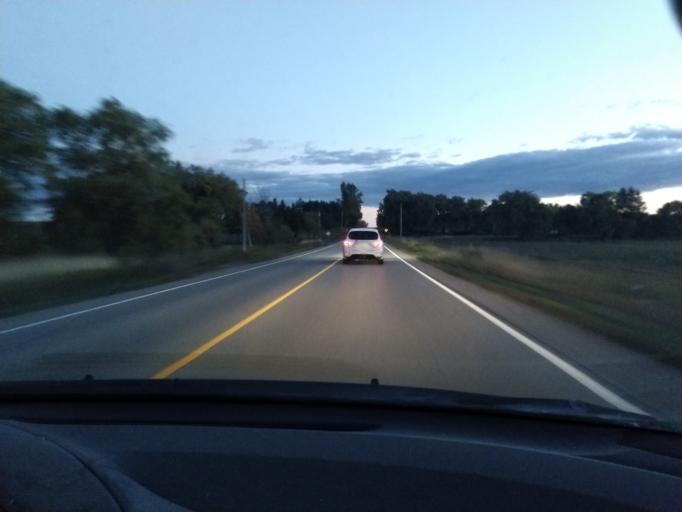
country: CA
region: Ontario
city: Bradford West Gwillimbury
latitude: 44.1335
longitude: -79.6478
